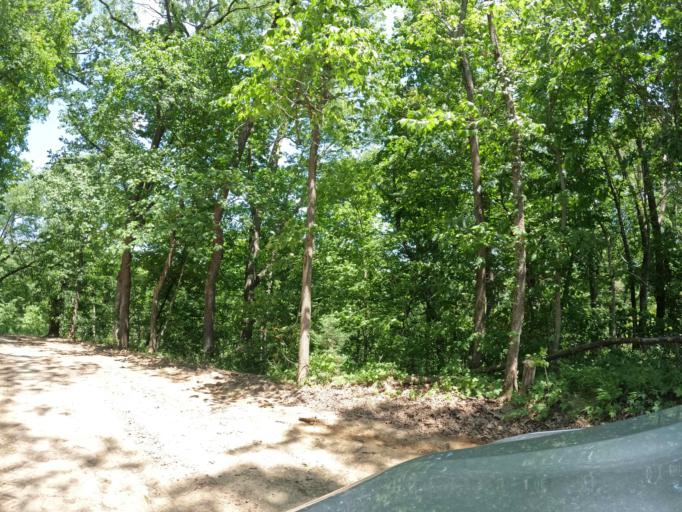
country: US
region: Iowa
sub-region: Henry County
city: Mount Pleasant
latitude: 40.9221
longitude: -91.6652
